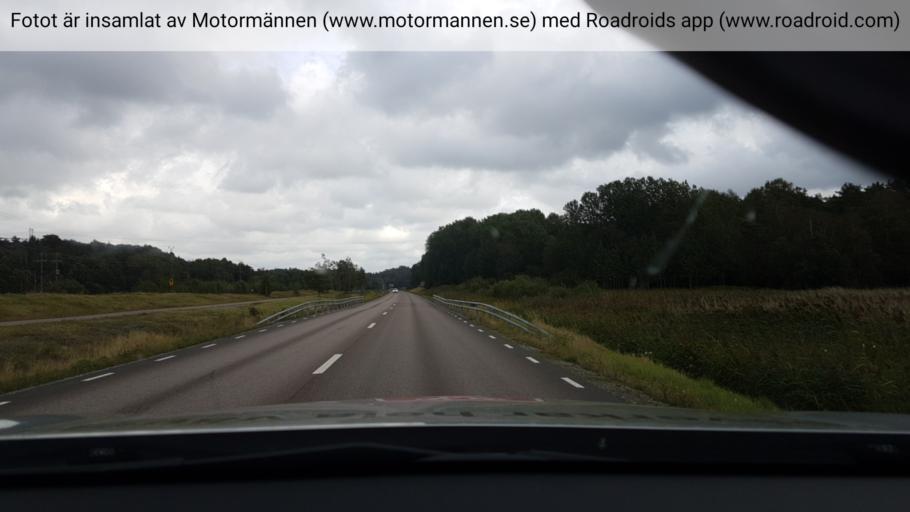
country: SE
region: Vaestra Goetaland
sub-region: Stromstads Kommun
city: Stroemstad
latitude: 58.9338
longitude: 11.1976
